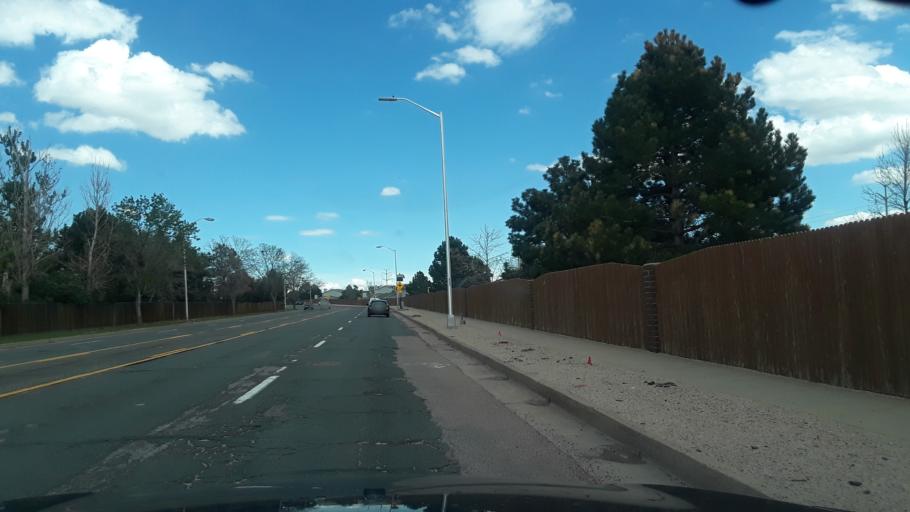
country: US
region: Colorado
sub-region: El Paso County
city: Black Forest
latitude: 38.9421
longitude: -104.7688
